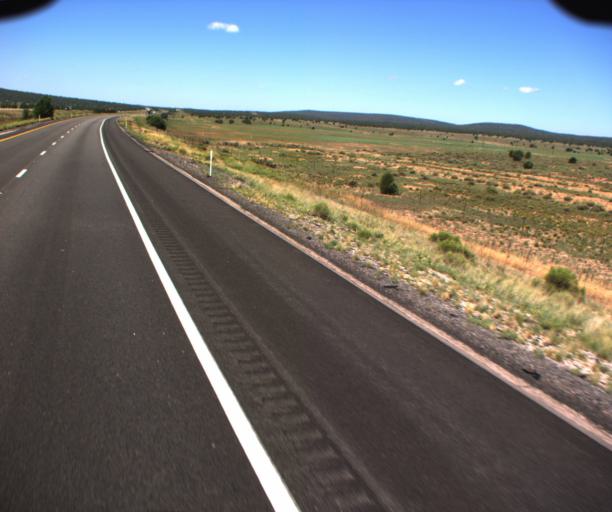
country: US
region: Arizona
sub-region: Mohave County
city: Peach Springs
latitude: 35.2355
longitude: -113.2104
